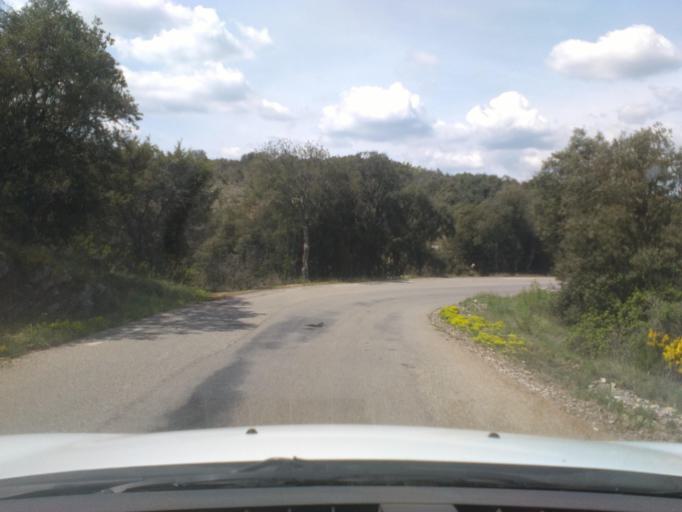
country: FR
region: Languedoc-Roussillon
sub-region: Departement du Gard
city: Saint-Hippolyte-du-Fort
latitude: 43.9775
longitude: 3.8894
